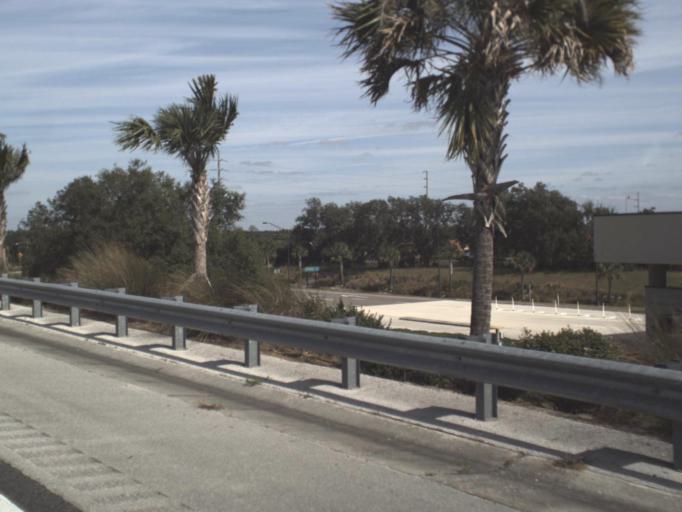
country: US
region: Florida
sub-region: Polk County
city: Citrus Ridge
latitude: 28.3450
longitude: -81.6161
